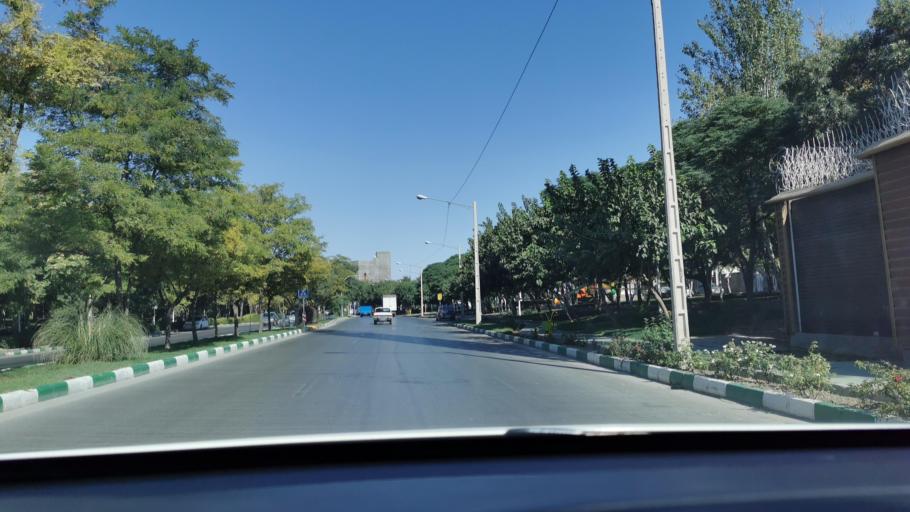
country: IR
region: Razavi Khorasan
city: Mashhad
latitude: 36.3342
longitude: 59.6357
